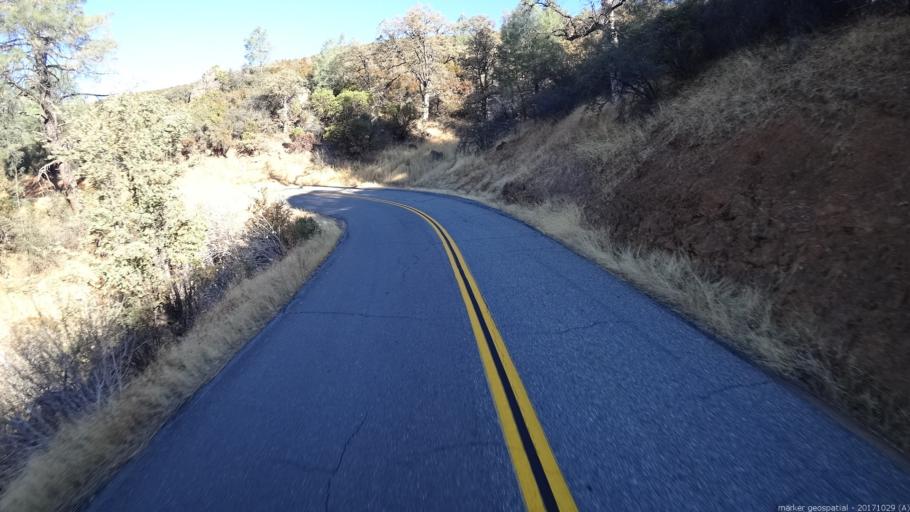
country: US
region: California
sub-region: Trinity County
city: Lewiston
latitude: 40.3681
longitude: -122.8713
